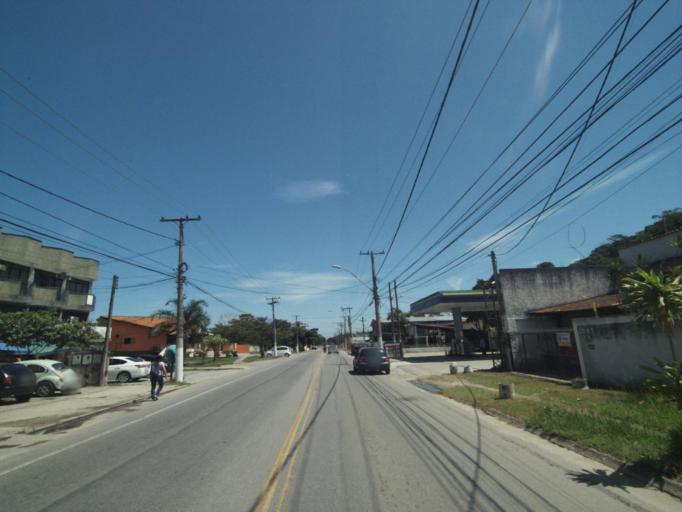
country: BR
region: Rio de Janeiro
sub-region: Niteroi
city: Niteroi
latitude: -22.9282
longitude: -43.0136
